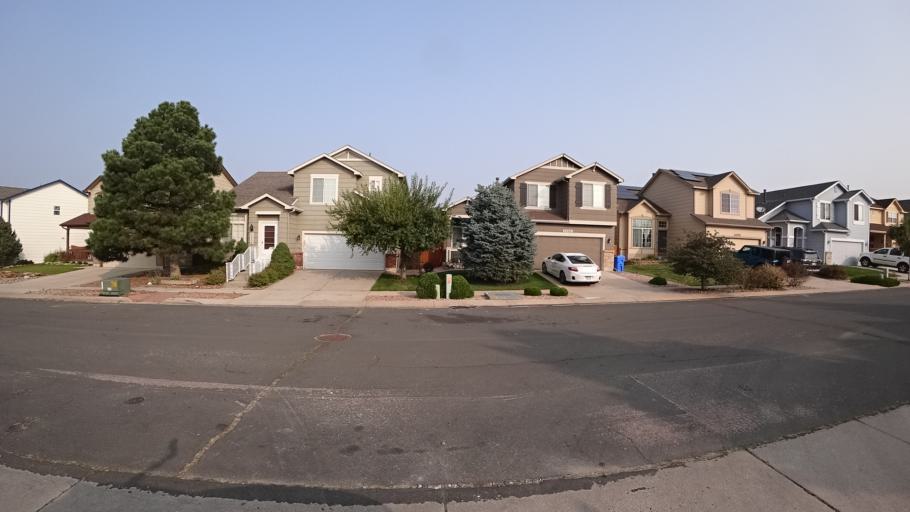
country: US
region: Colorado
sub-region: El Paso County
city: Cimarron Hills
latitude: 38.9328
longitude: -104.7266
